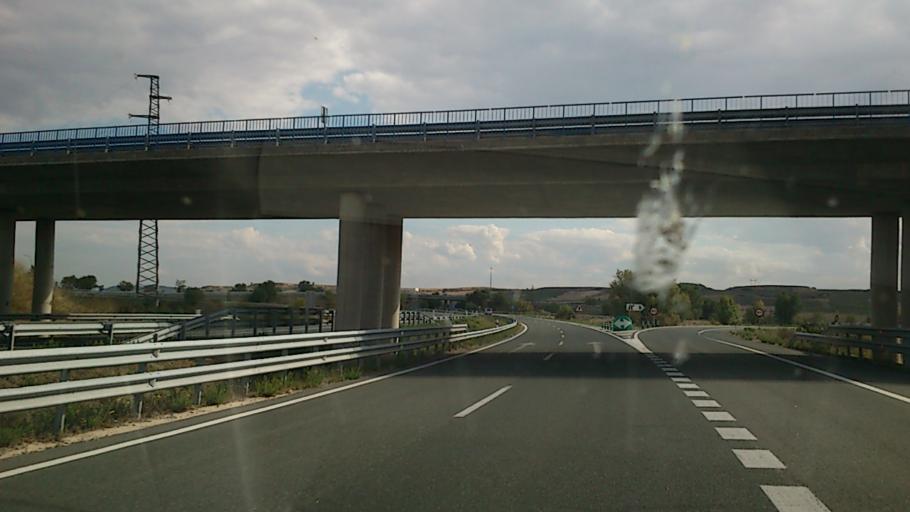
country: ES
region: La Rioja
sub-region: Provincia de La Rioja
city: Anguciana
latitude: 42.5625
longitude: -2.8787
